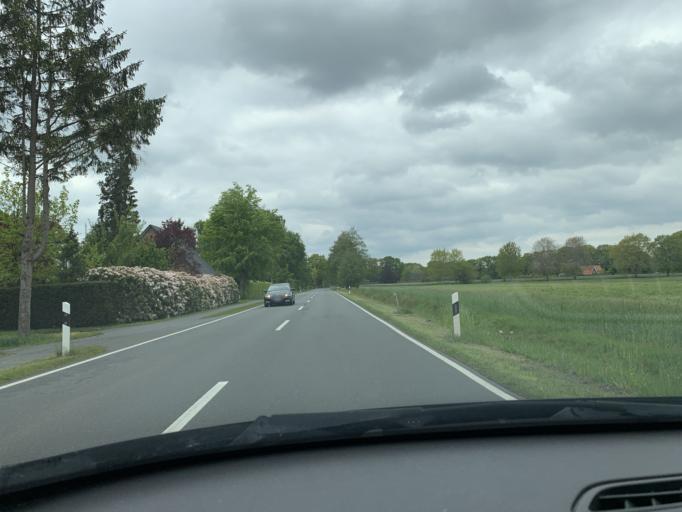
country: DE
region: Lower Saxony
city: Bad Zwischenahn
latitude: 53.1891
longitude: 8.0585
